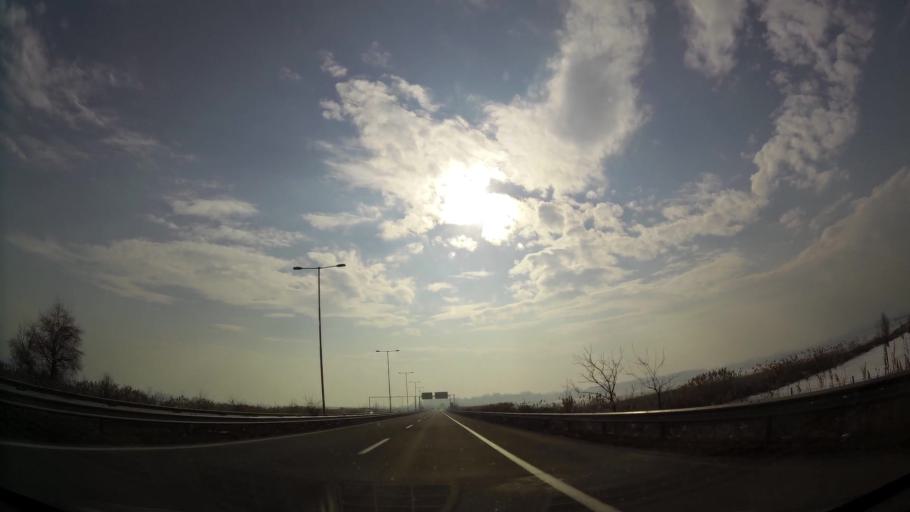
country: MK
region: Aracinovo
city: Arachinovo
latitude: 42.0022
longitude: 21.5339
